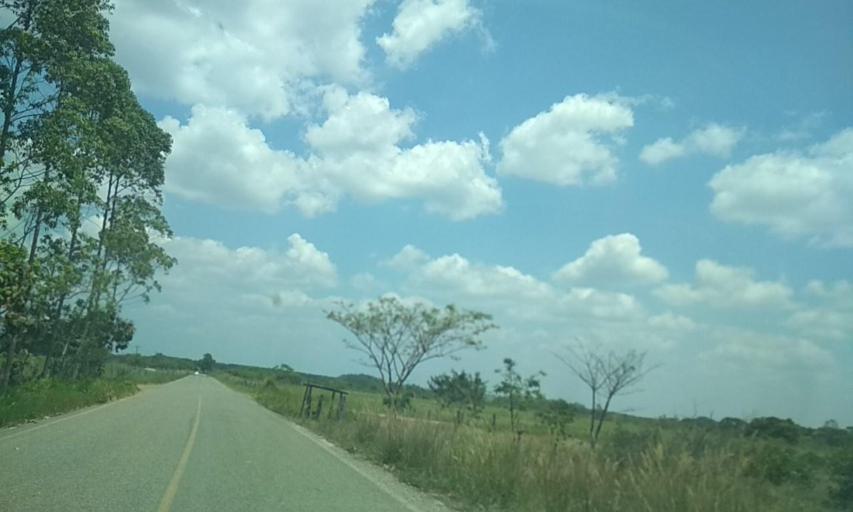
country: MX
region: Tabasco
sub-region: Huimanguillo
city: Huapacal 1ra. Seccion
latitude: 17.7582
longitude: -93.7778
